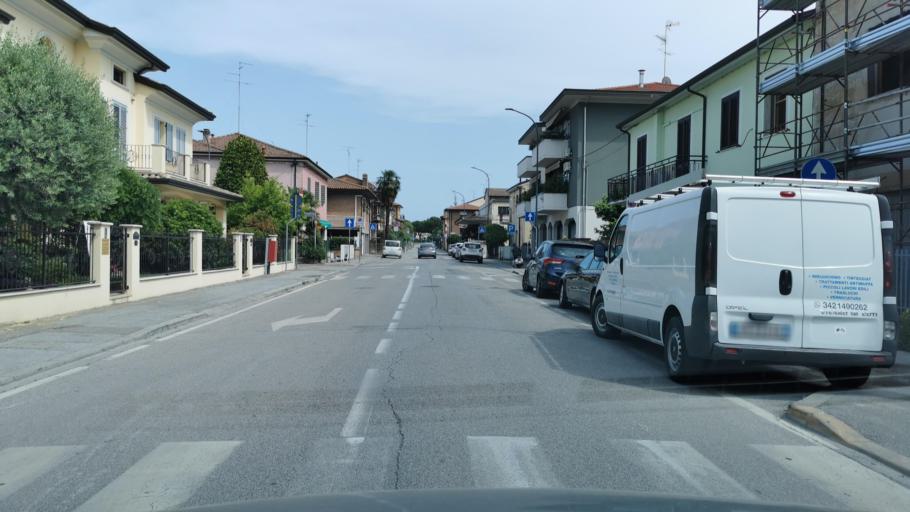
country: IT
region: Emilia-Romagna
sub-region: Provincia di Ravenna
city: Ravenna
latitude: 44.4162
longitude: 12.1848
